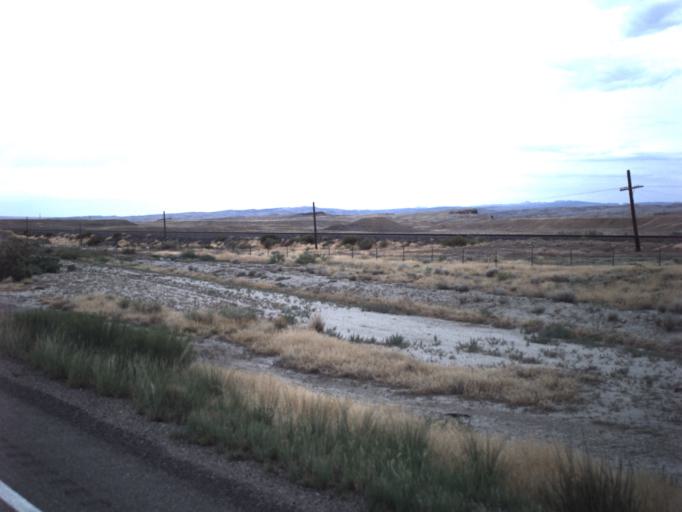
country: US
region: Utah
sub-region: Carbon County
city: East Carbon City
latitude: 39.3771
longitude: -110.4030
